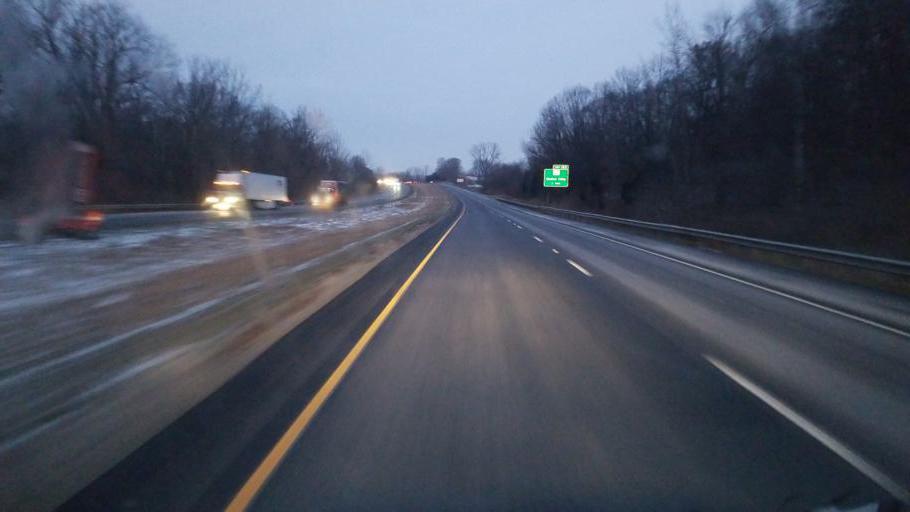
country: US
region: Ohio
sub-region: Preble County
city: New Paris
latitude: 39.8583
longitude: -84.8432
